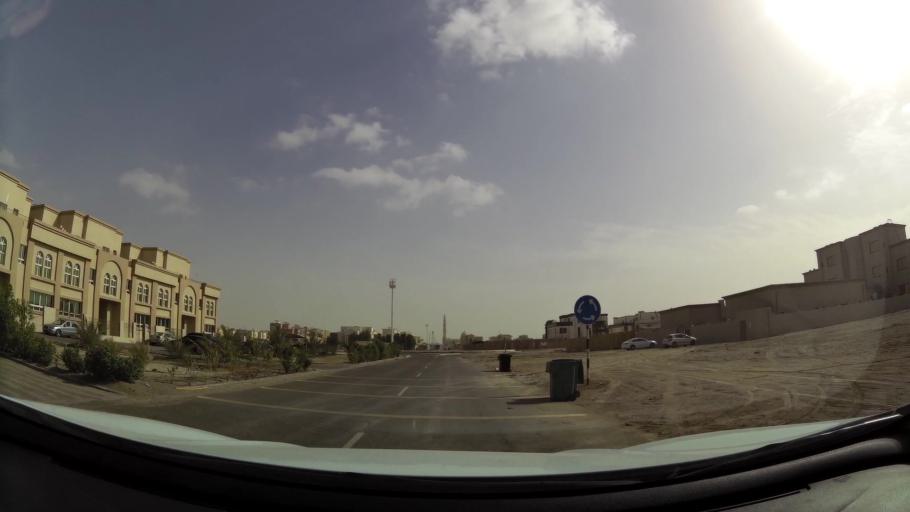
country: AE
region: Abu Dhabi
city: Abu Dhabi
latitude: 24.4340
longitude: 54.5917
